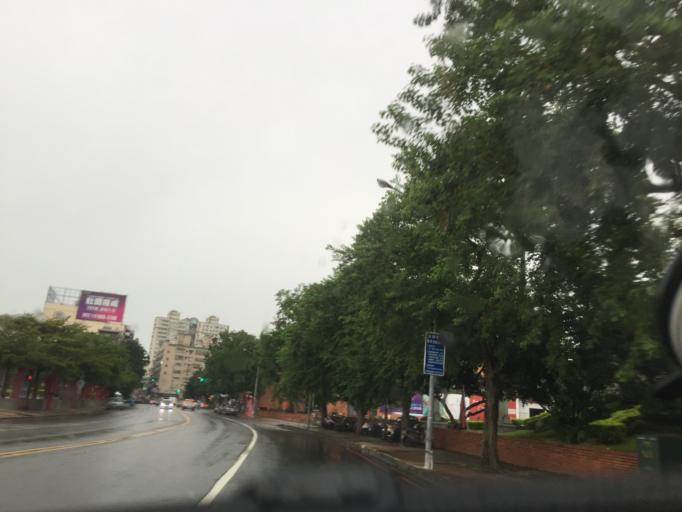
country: TW
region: Taiwan
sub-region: Hsinchu
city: Zhubei
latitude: 24.8298
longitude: 121.0112
